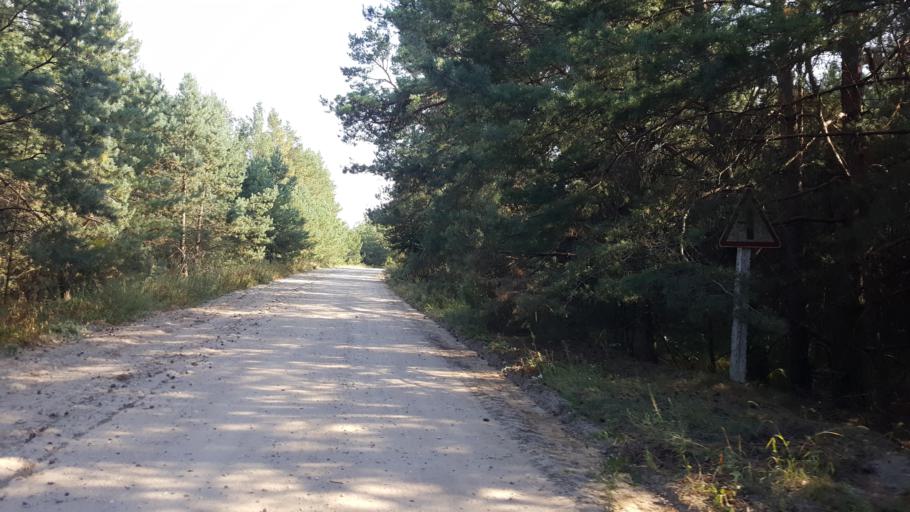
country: BY
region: Brest
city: Kamyanyuki
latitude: 52.5532
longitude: 23.6487
